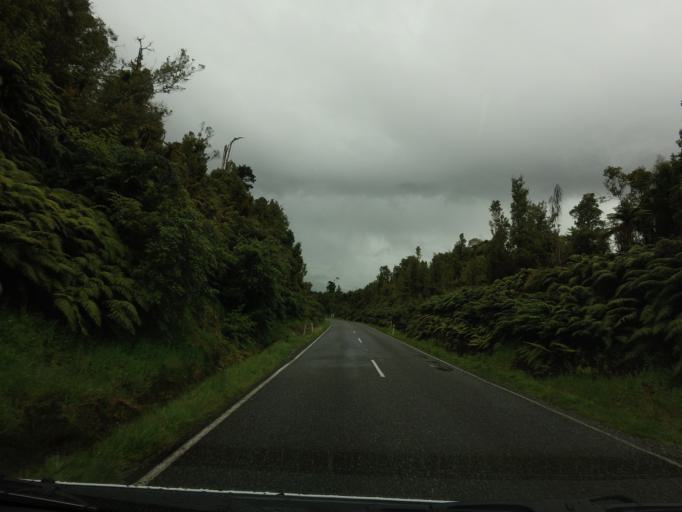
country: NZ
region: West Coast
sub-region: Westland District
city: Hokitika
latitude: -43.0464
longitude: 170.6384
